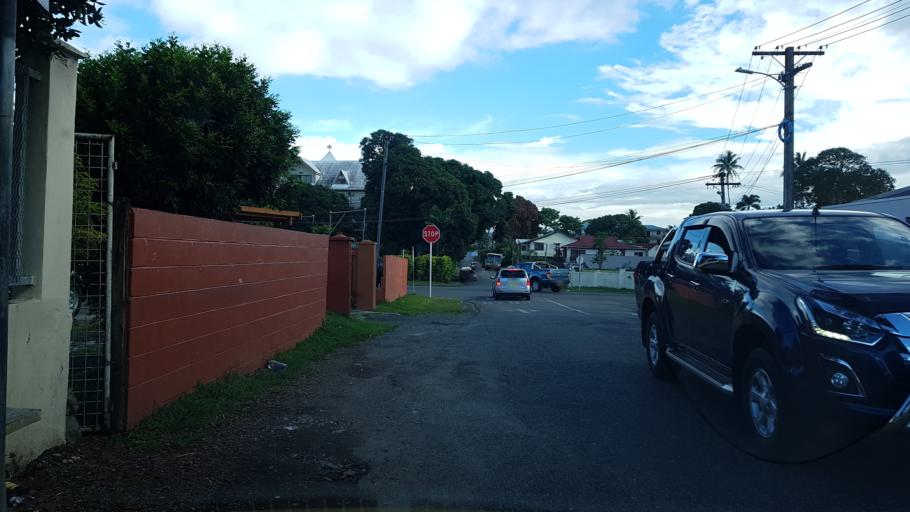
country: FJ
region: Central
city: Suva
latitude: -18.1468
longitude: 178.4297
